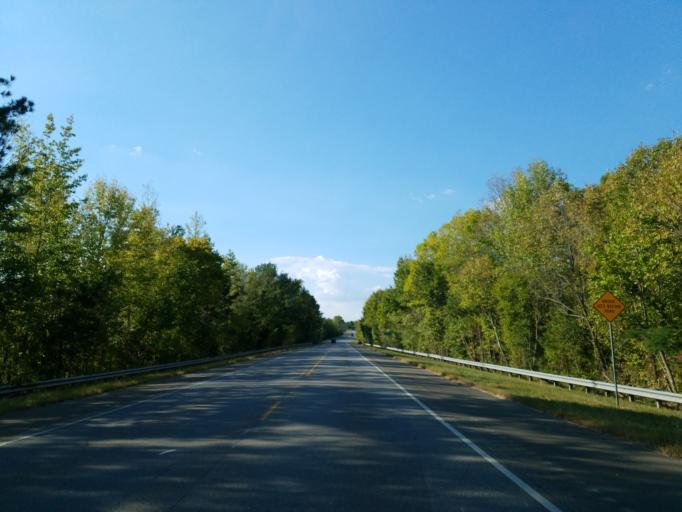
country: US
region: Georgia
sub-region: Murray County
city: Chatsworth
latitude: 34.6913
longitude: -84.7343
